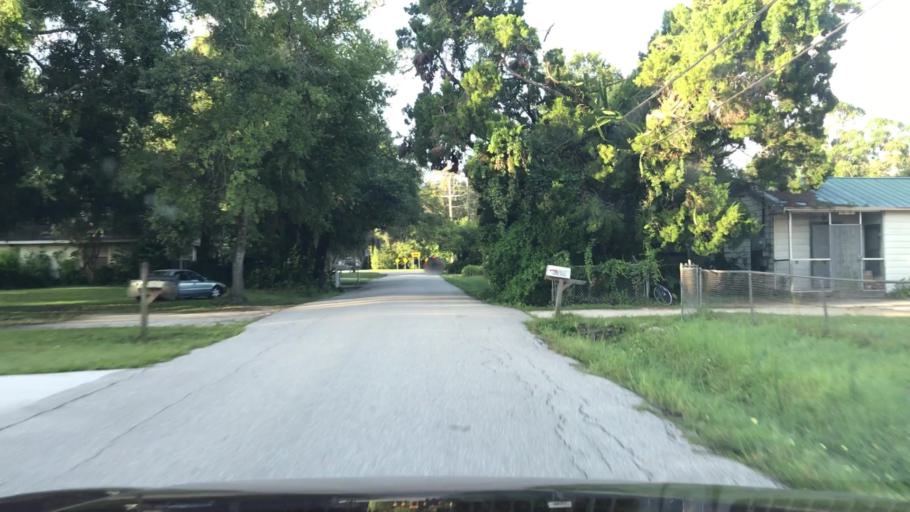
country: US
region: Florida
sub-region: Sarasota County
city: Fruitville
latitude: 27.3242
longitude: -82.4593
